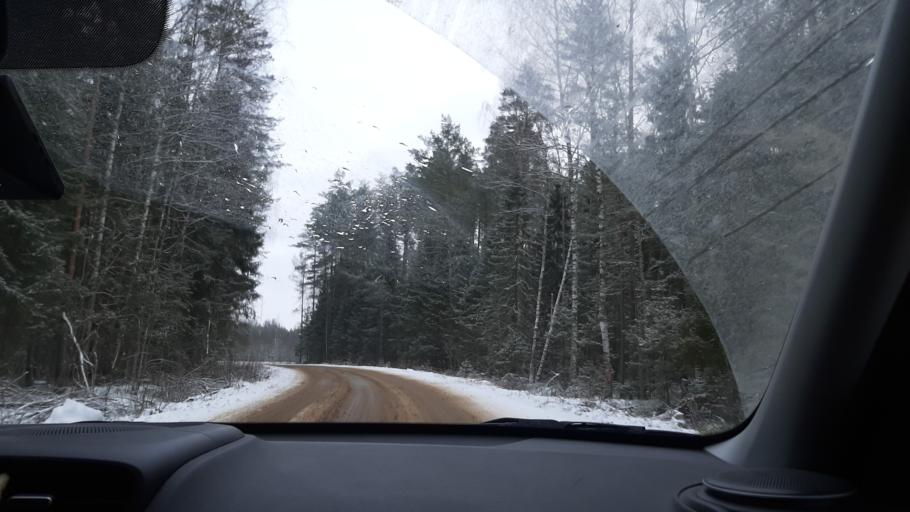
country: RU
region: Ivanovo
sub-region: Gorod Ivanovo
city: Ivanovo
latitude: 56.9159
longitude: 41.0028
